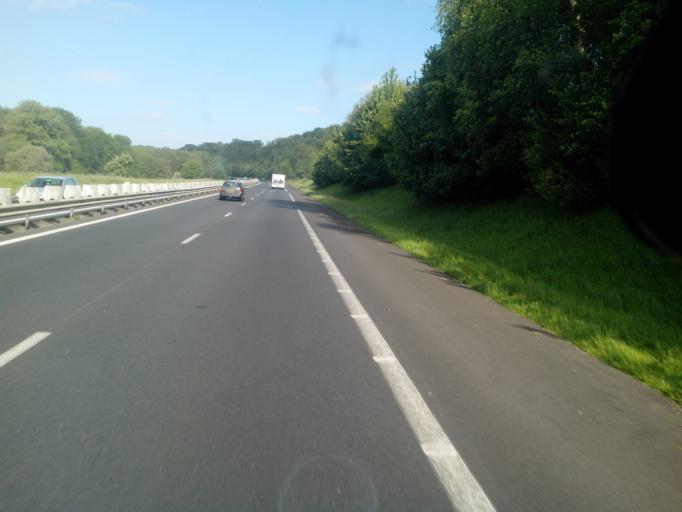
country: FR
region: Lower Normandy
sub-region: Departement du Calvados
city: Dozule
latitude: 49.2462
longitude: 0.0390
